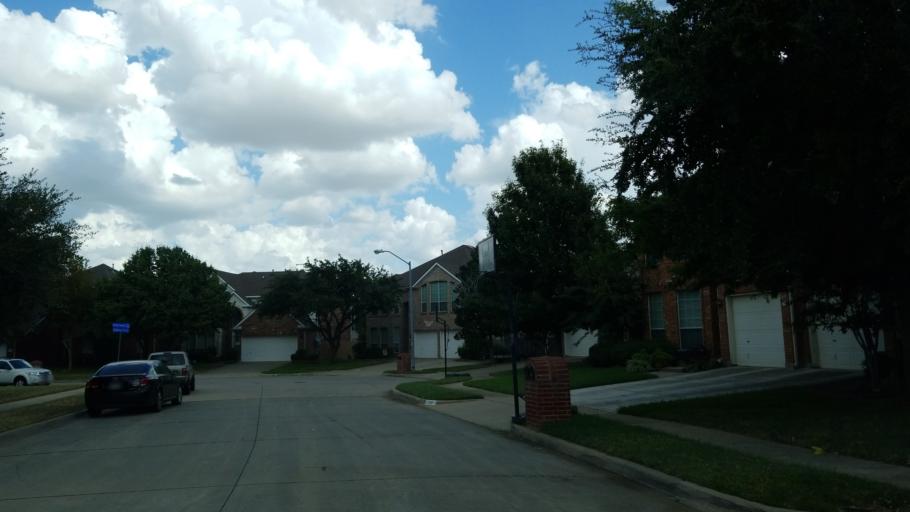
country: US
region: Texas
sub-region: Tarrant County
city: Euless
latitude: 32.8791
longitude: -97.0801
